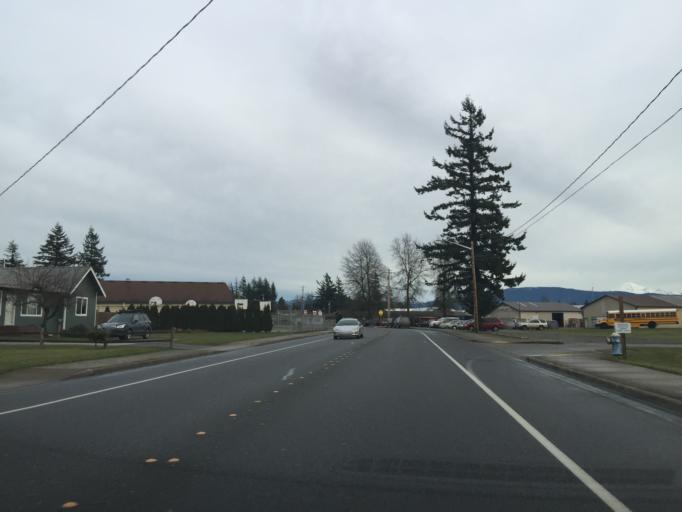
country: US
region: Washington
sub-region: Whatcom County
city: Lynden
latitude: 48.9482
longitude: -122.4478
